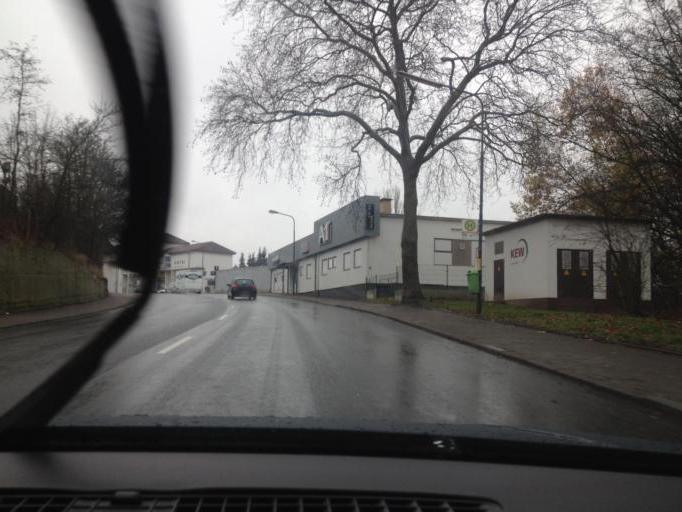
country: DE
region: Saarland
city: Neunkirchen
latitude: 49.3386
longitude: 7.1890
